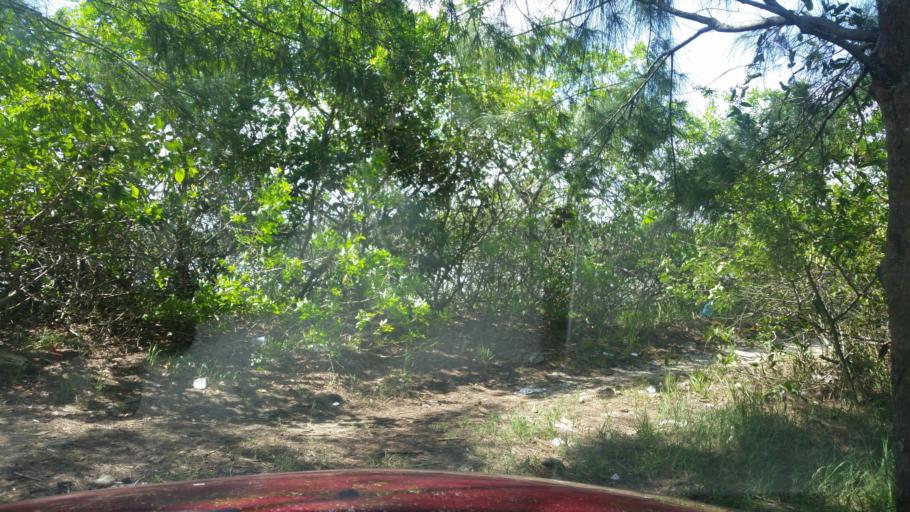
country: BR
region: Sao Paulo
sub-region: Iguape
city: Iguape
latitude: -24.6932
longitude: -47.4530
